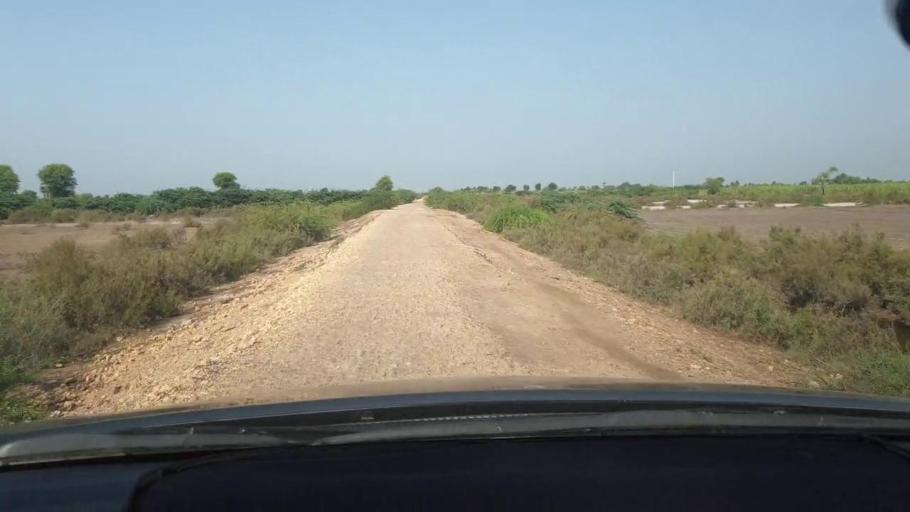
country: PK
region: Sindh
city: Tando Bago
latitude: 24.6800
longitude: 69.1367
